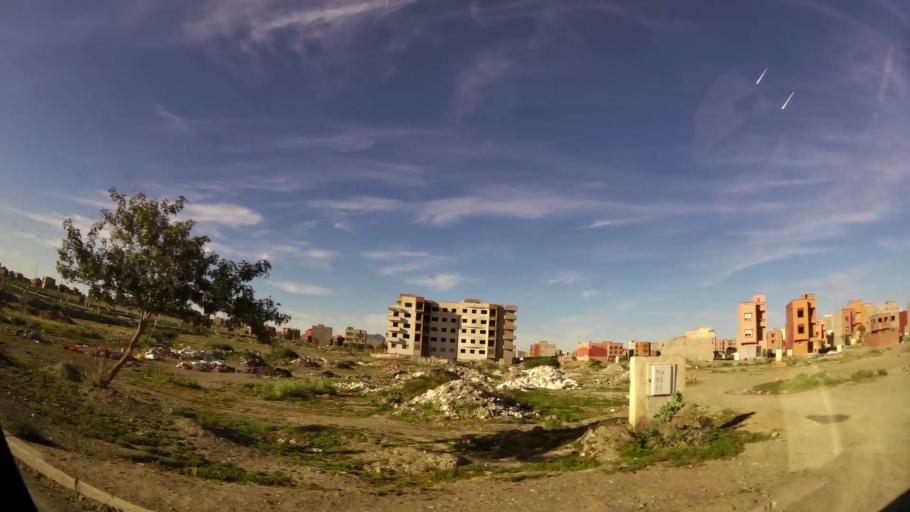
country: MA
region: Marrakech-Tensift-Al Haouz
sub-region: Marrakech
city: Marrakesh
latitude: 31.7628
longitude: -8.1050
